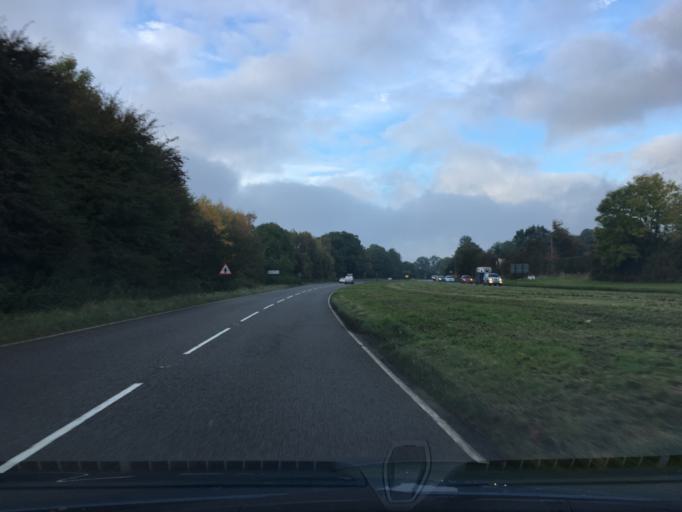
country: GB
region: England
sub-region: Hampshire
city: Long Sutton
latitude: 51.1734
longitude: -0.9198
